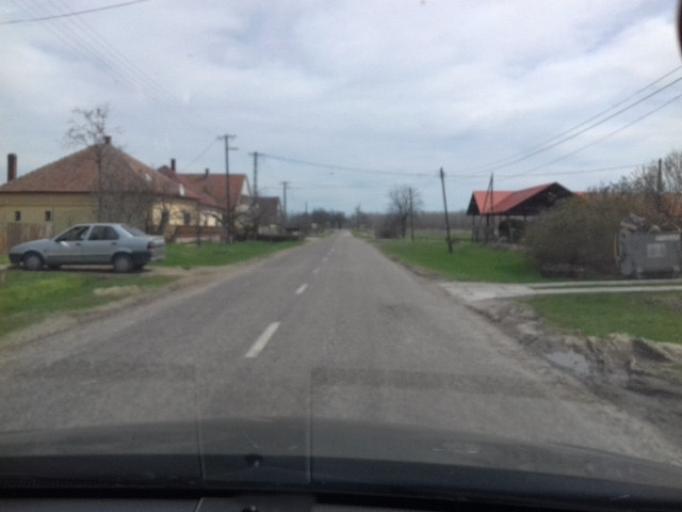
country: HU
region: Jasz-Nagykun-Szolnok
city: Cserkeszolo
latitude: 46.9038
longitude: 20.1605
